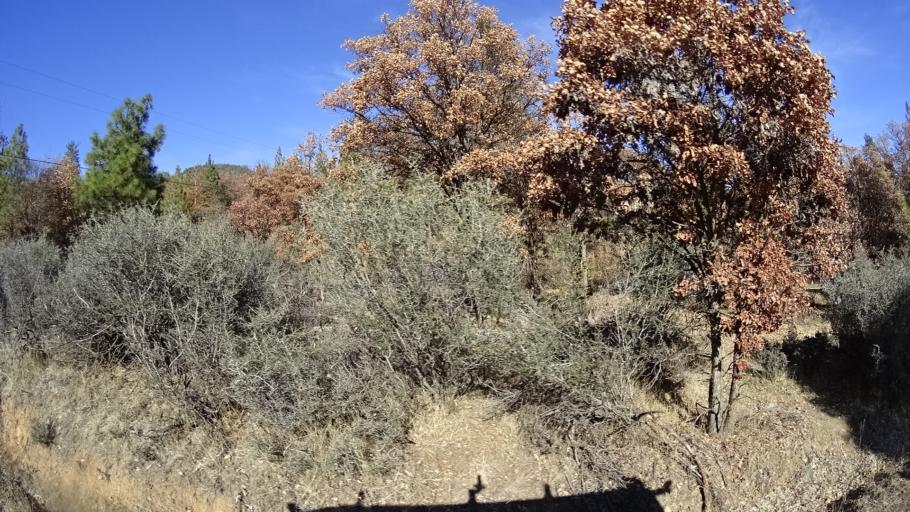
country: US
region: California
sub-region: Siskiyou County
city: Yreka
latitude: 41.7210
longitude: -122.6896
